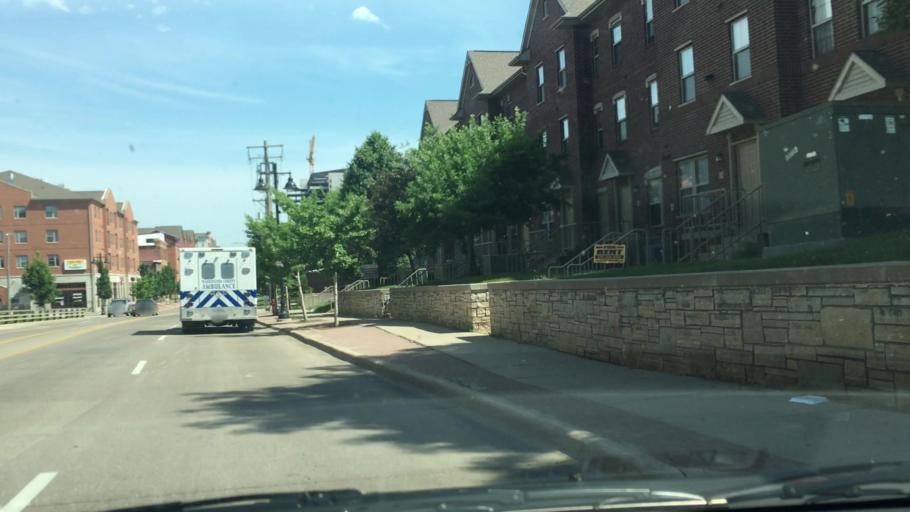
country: US
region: Iowa
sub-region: Johnson County
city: Iowa City
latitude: 41.6547
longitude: -91.5301
